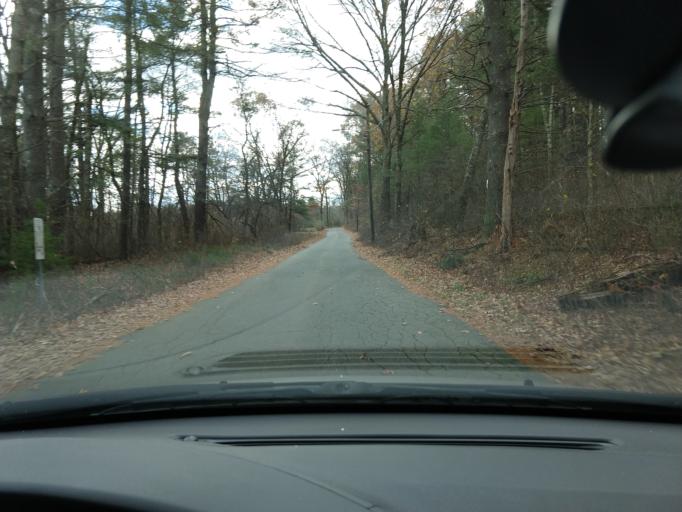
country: US
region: Massachusetts
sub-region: Middlesex County
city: Wayland
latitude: 42.3997
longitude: -71.3755
